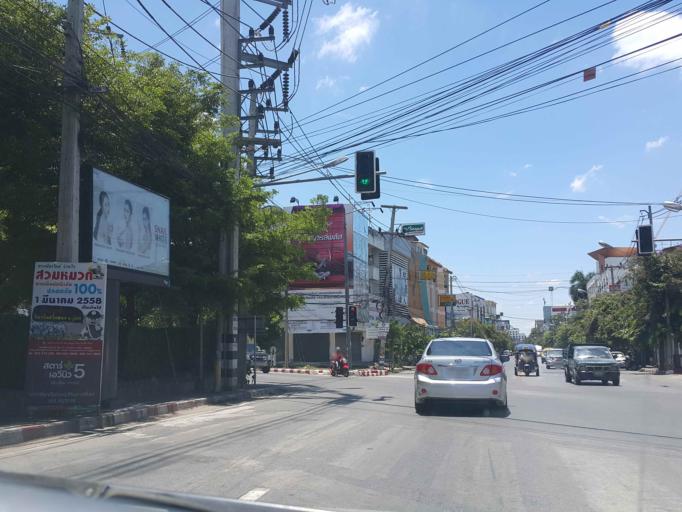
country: TH
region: Chiang Mai
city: Chiang Mai
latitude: 18.7736
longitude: 98.9989
